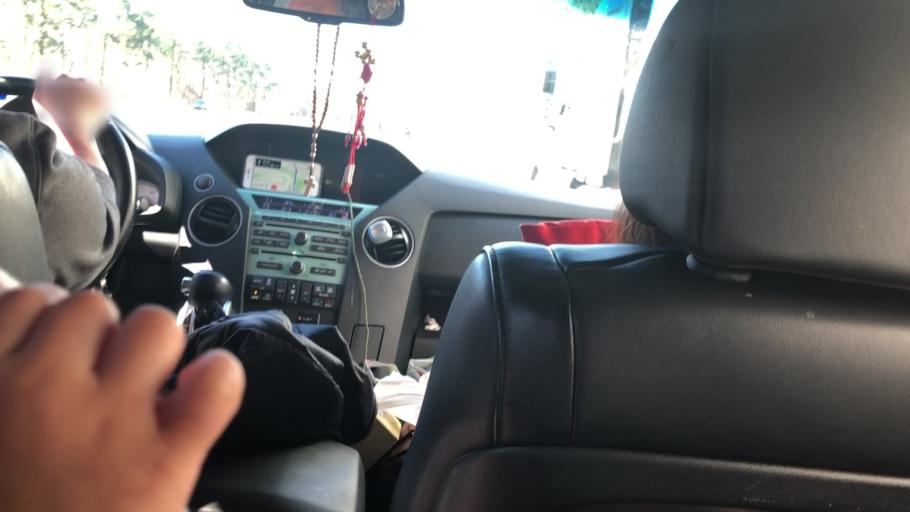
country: US
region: Louisiana
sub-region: Saint John the Baptist Parish
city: Laplace
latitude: 30.1013
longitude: -90.4843
